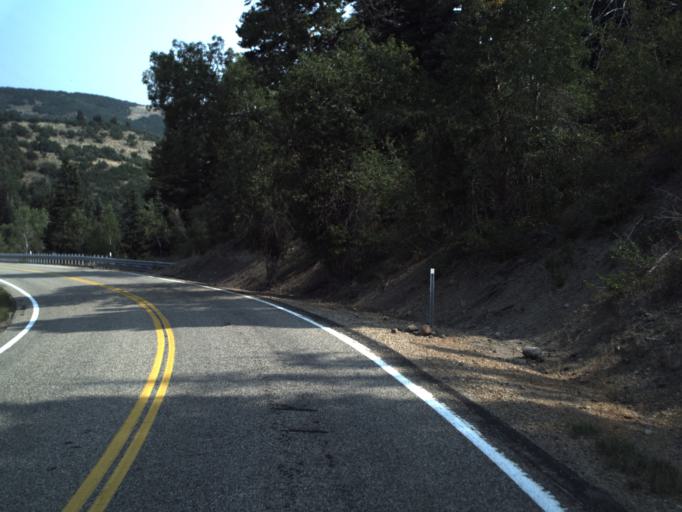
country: US
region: Utah
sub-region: Summit County
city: Summit Park
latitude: 40.8492
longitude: -111.6251
